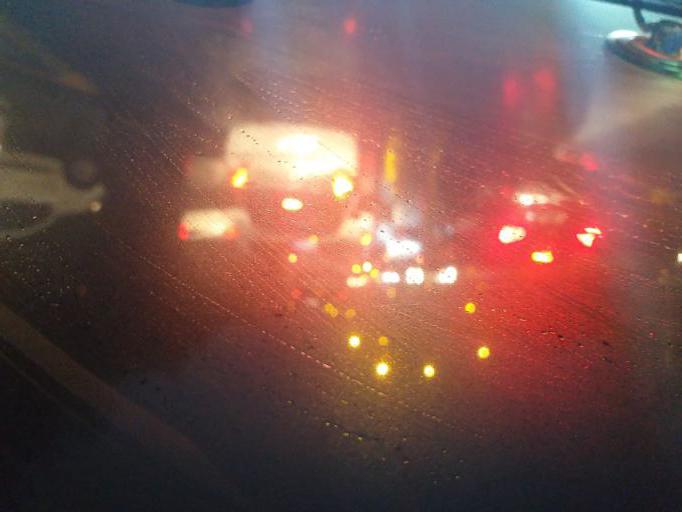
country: TR
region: Ankara
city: Ankara
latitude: 39.9538
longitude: 32.8210
